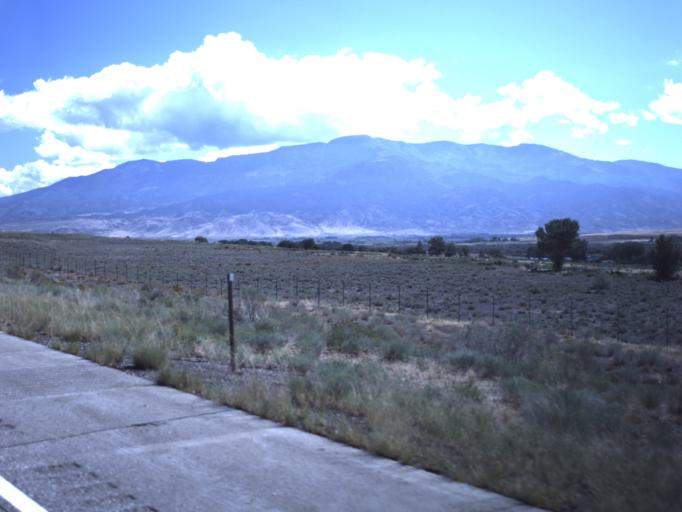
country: US
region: Utah
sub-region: Sevier County
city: Monroe
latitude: 38.6570
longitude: -112.2020
